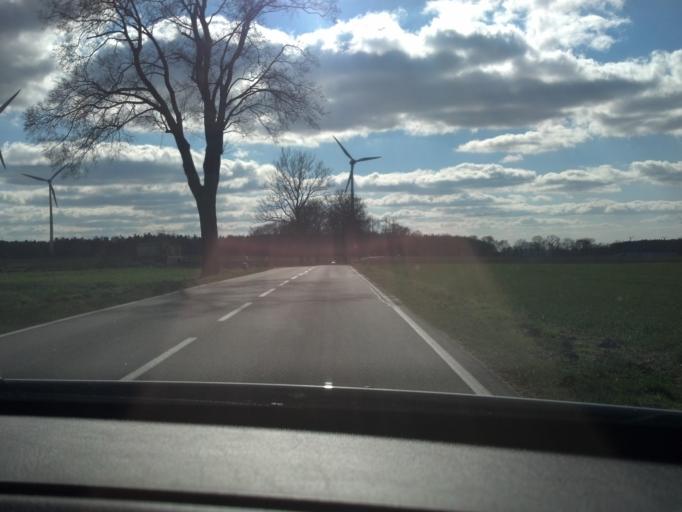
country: DE
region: Brandenburg
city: Gerdshagen
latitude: 53.3015
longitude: 12.2202
